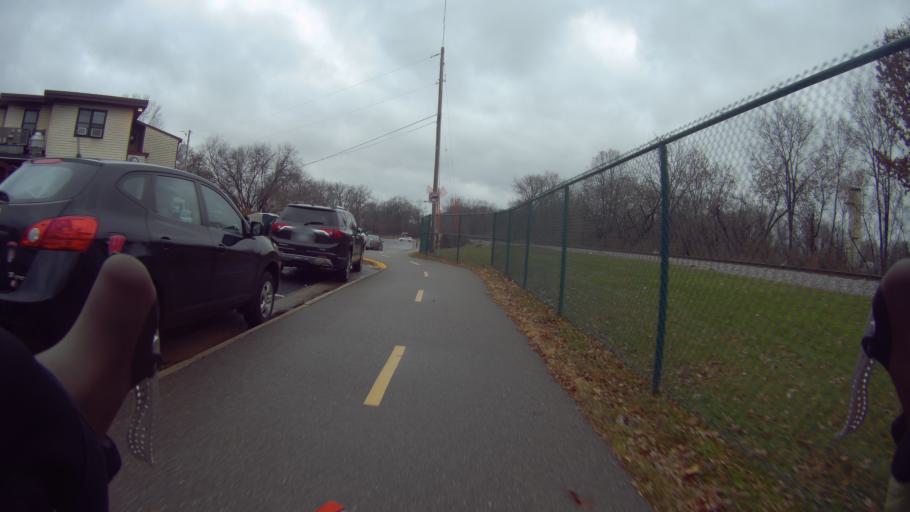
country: US
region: Wisconsin
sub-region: Dane County
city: McFarland
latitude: 43.0260
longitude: -89.3060
